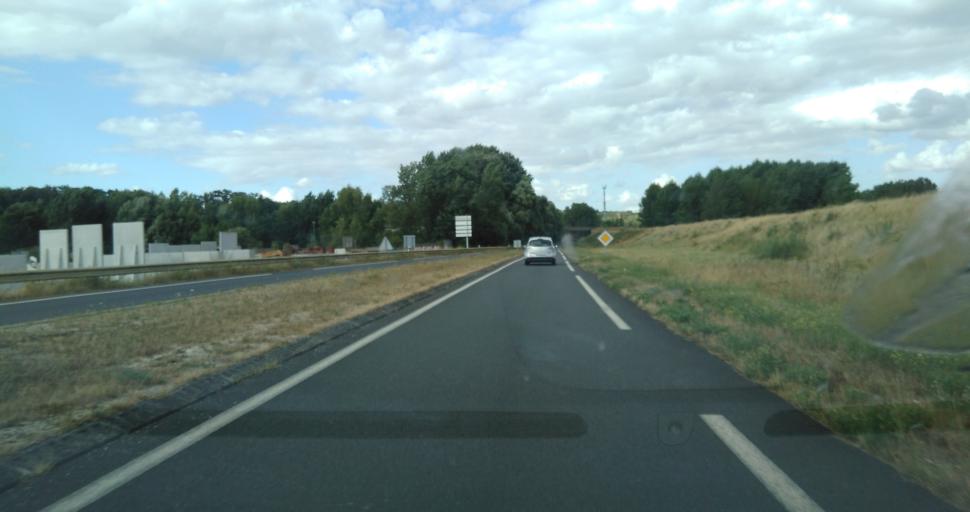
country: FR
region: Centre
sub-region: Departement d'Indre-et-Loire
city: Cinq-Mars-la-Pile
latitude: 47.3442
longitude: 0.4669
